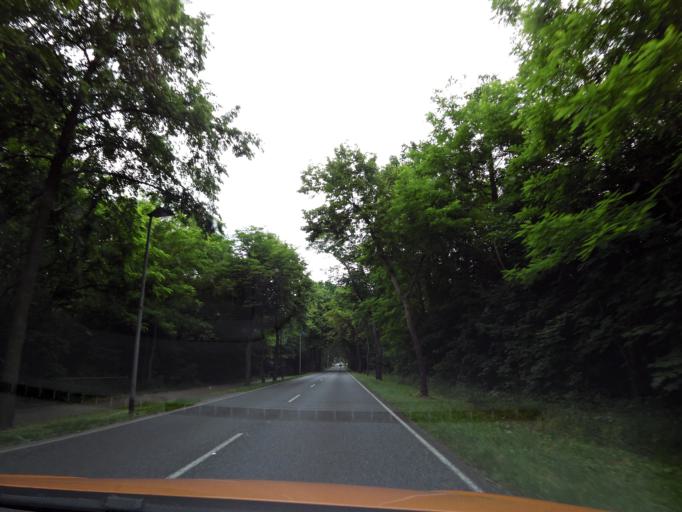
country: DE
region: Brandenburg
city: Zossen
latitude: 52.1536
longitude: 13.4785
